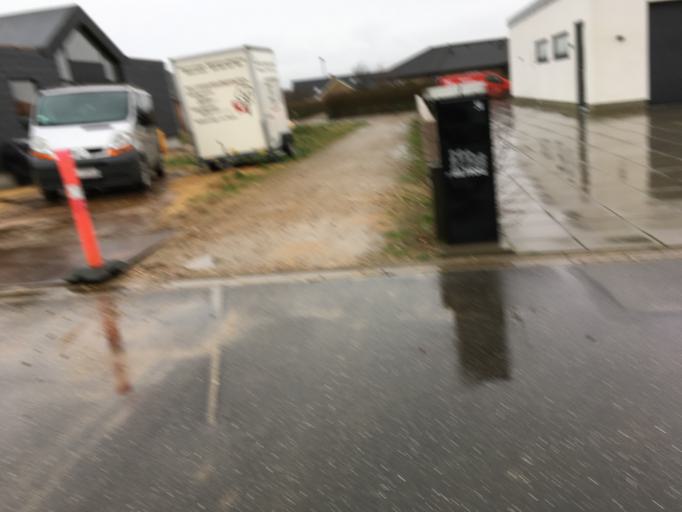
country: DK
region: Central Jutland
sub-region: Ringkobing-Skjern Kommune
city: Ringkobing
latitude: 56.1006
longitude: 8.2627
